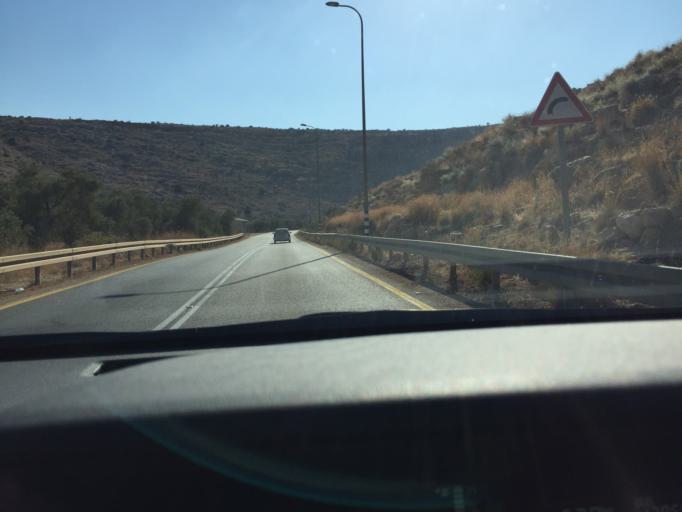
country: PS
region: West Bank
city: Al Lubban al Gharbi
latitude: 32.0492
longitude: 35.0457
